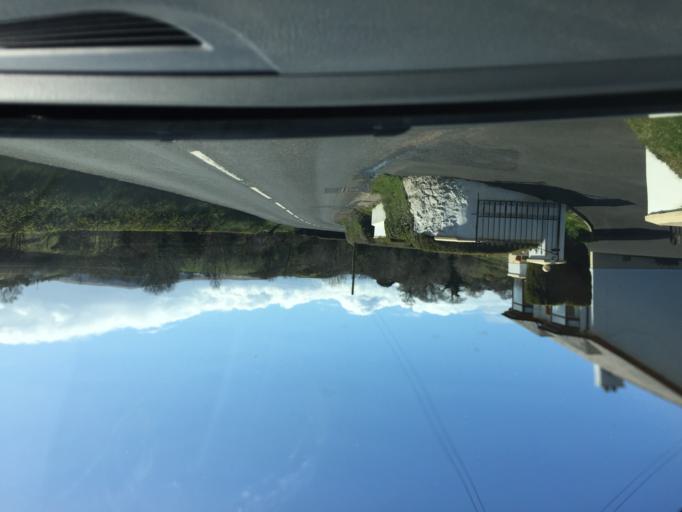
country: GB
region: Northern Ireland
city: Cushendall
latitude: 55.0838
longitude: -6.0759
